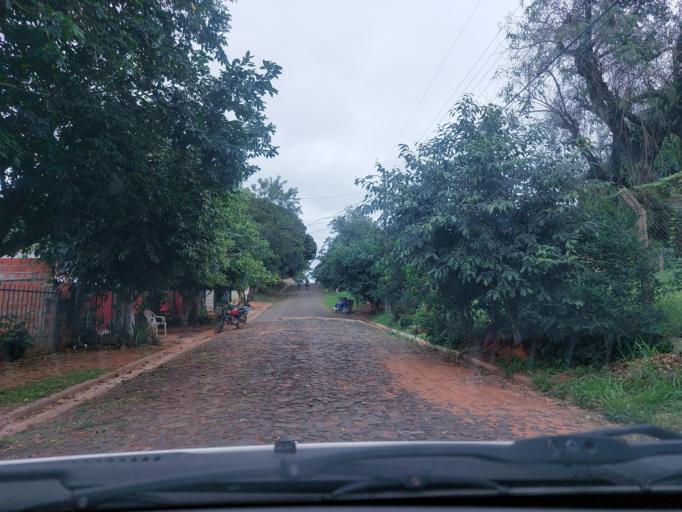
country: PY
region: San Pedro
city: Guayaybi
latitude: -24.6740
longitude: -56.4401
